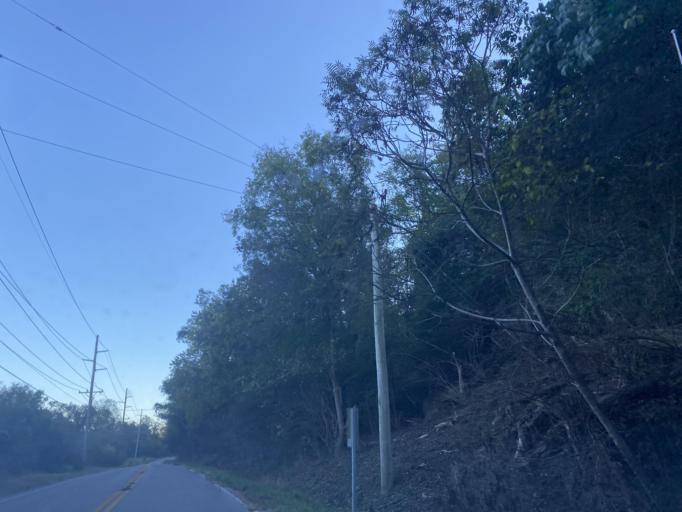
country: US
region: Kentucky
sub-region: Campbell County
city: Fort Thomas
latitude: 39.1024
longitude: -84.4417
